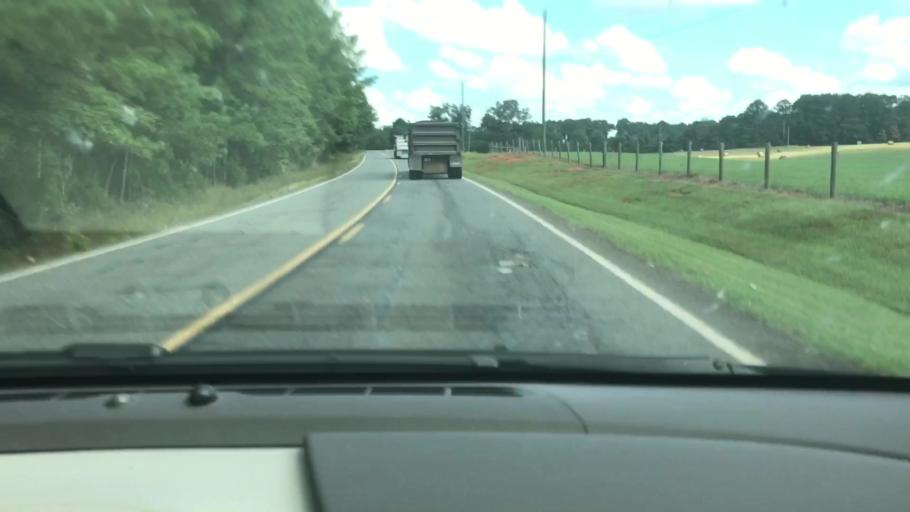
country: US
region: Alabama
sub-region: Chambers County
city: Valley
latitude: 32.8493
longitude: -85.0356
